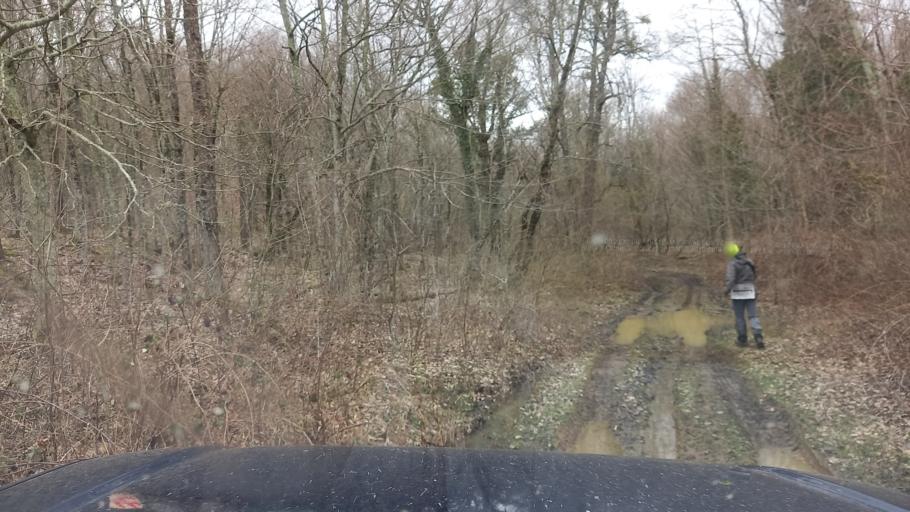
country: RU
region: Krasnodarskiy
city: Pshada
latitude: 44.4897
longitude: 38.3935
